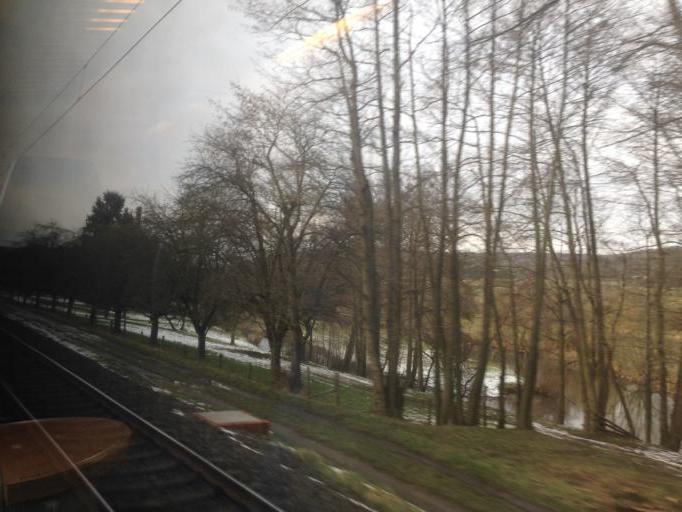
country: DE
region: Hesse
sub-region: Regierungsbezirk Giessen
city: Sinn
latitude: 50.6201
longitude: 8.3362
